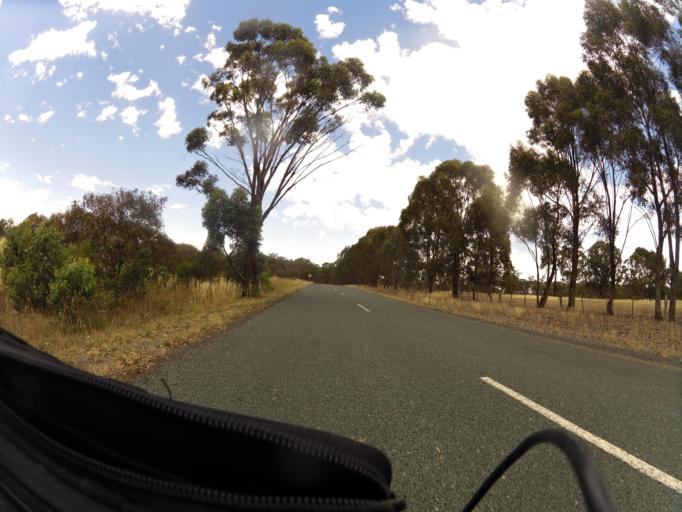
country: AU
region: Victoria
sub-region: Greater Shepparton
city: Shepparton
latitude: -36.6434
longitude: 145.2103
